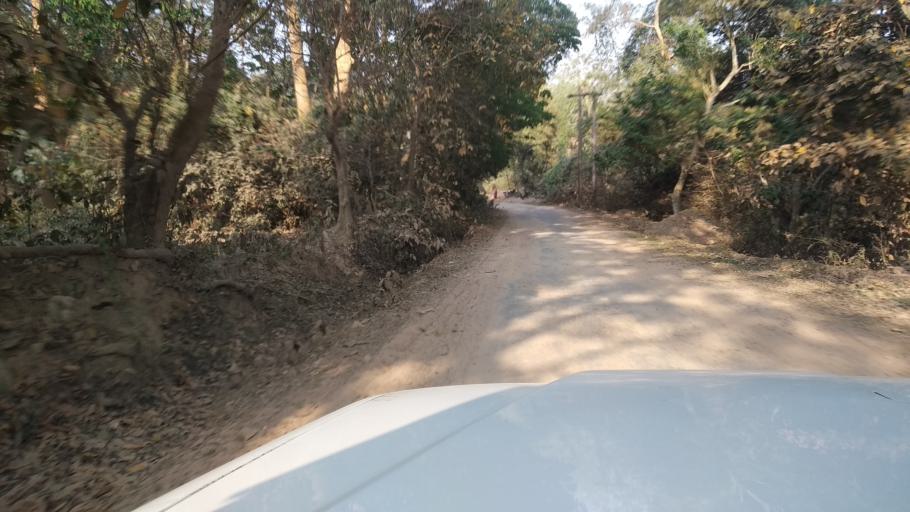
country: IN
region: Tripura
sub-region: West Tripura
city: Sonamura
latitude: 23.4211
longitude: 91.2896
